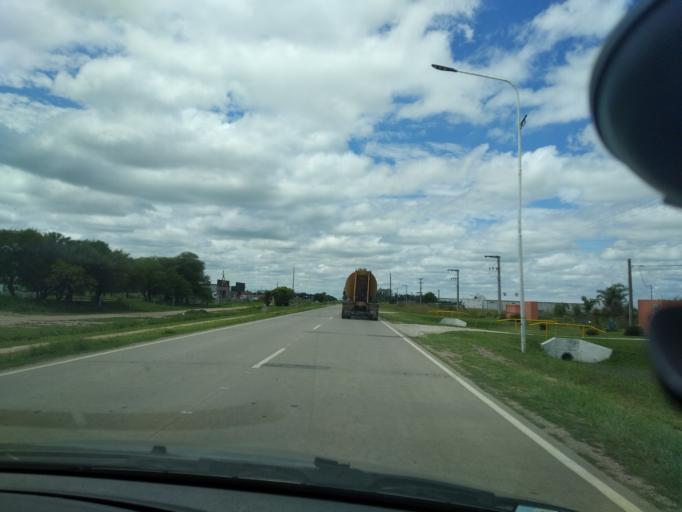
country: AR
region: Cordoba
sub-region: Departamento de Rio Segundo
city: Rio Segundo
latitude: -31.6406
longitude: -63.8950
